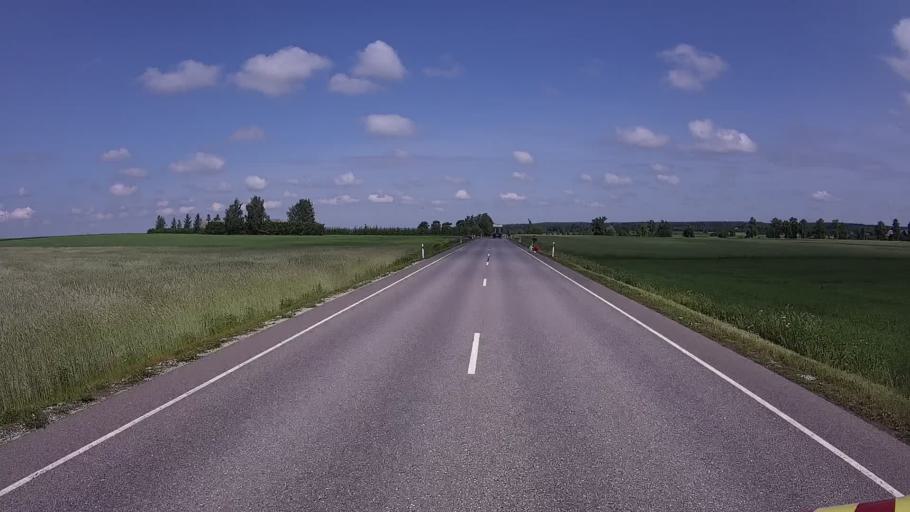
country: EE
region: Tartu
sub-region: UElenurme vald
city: Ulenurme
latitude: 58.2337
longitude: 26.7883
